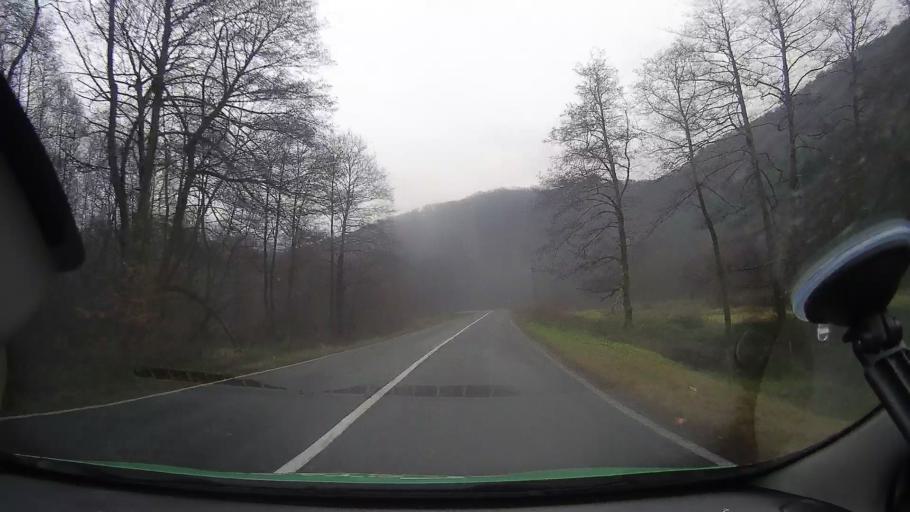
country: RO
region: Arad
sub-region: Comuna Plescuta
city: Plescuta
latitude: 46.3170
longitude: 22.4662
